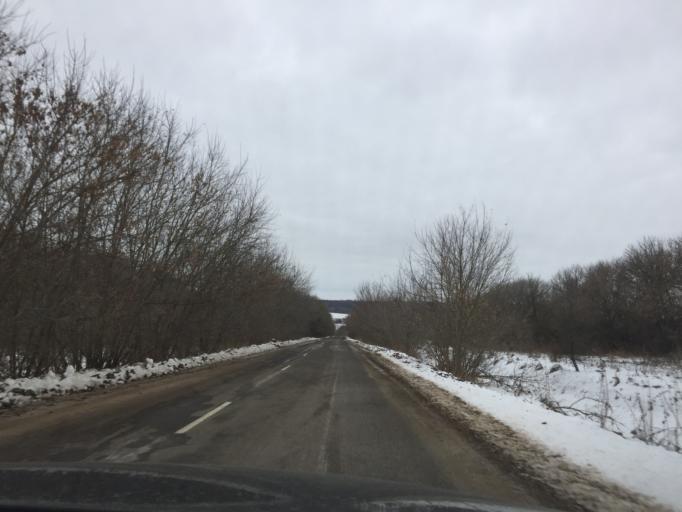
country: RU
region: Tula
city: Teploye
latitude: 53.7789
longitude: 37.6330
